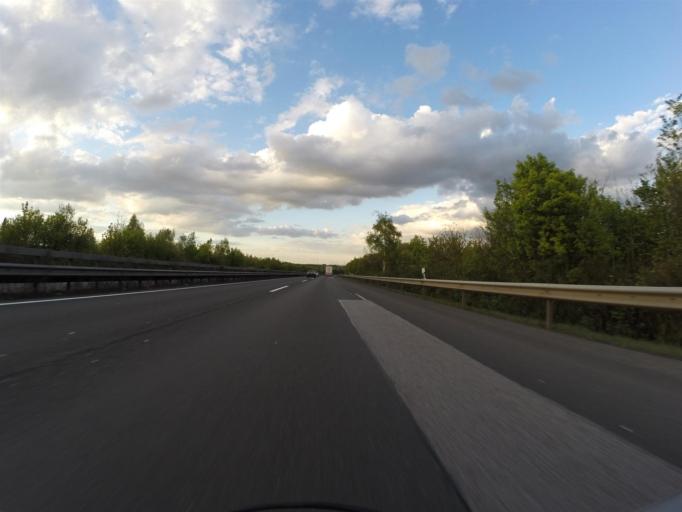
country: DE
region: Rheinland-Pfalz
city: Lonsheim
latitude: 49.7600
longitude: 8.0902
